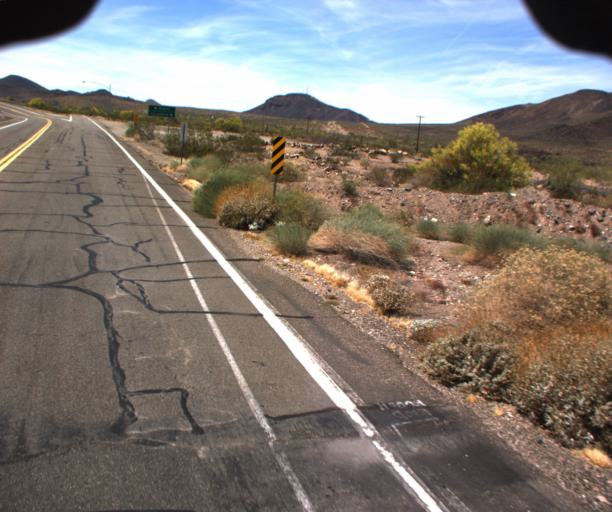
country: US
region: Arizona
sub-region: La Paz County
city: Quartzsite
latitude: 33.6647
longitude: -114.0062
